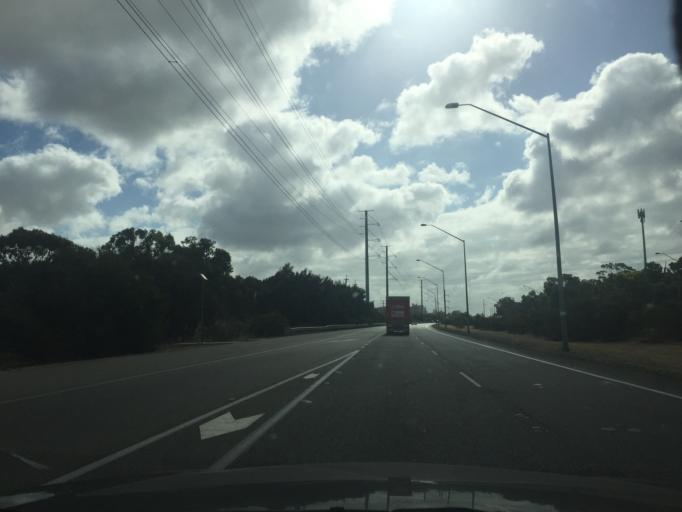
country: AU
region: Western Australia
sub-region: Canning
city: Canning Vale
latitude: -32.0545
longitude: 115.9284
